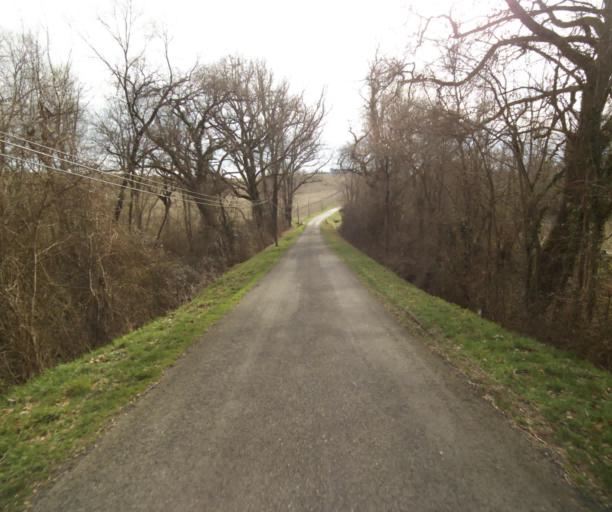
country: FR
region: Aquitaine
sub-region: Departement des Landes
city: Gabarret
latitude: 43.9426
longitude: 0.0465
